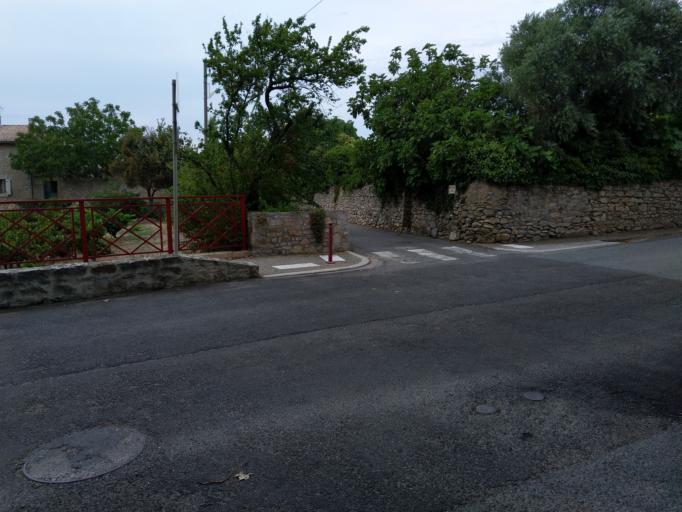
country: FR
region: Languedoc-Roussillon
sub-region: Departement de l'Herault
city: Olonzac
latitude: 43.2989
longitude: 2.7585
